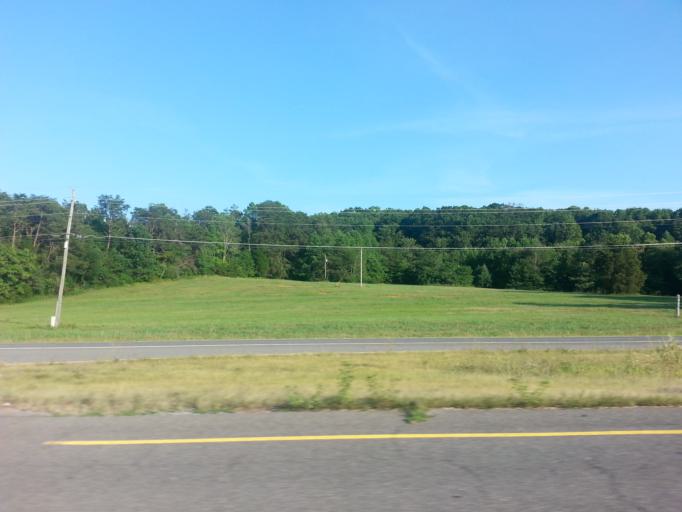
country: US
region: Tennessee
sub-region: Monroe County
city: Madisonville
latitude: 35.5478
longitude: -84.3182
